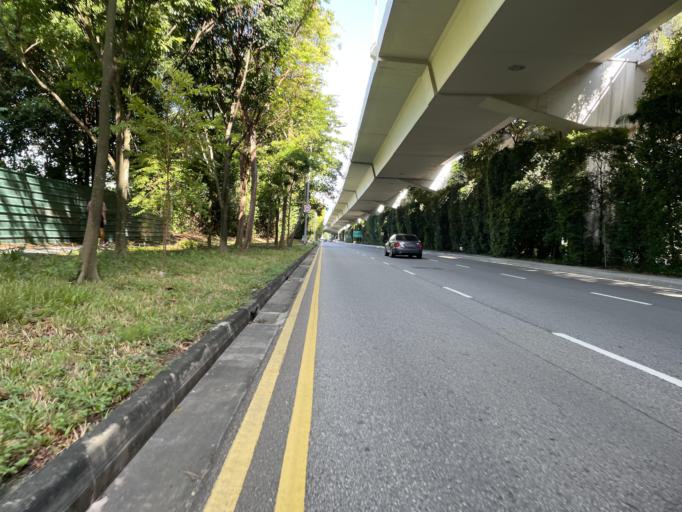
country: SG
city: Singapore
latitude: 1.2771
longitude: 103.7891
